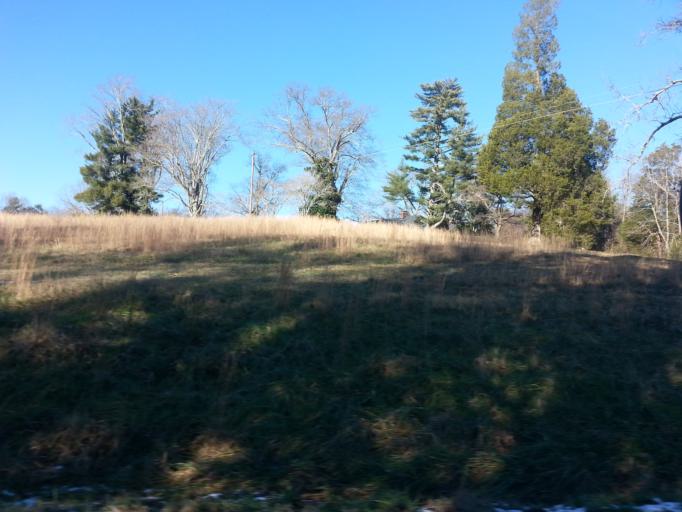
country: US
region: Tennessee
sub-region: Blount County
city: Louisville
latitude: 35.8893
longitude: -83.9856
